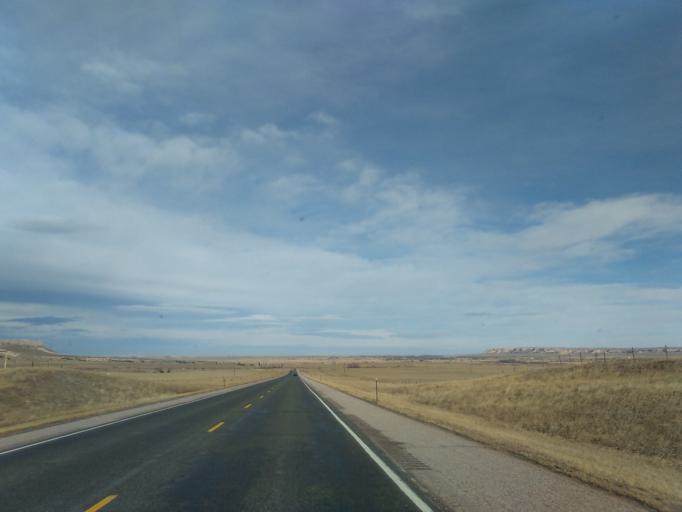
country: US
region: Wyoming
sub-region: Goshen County
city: Torrington
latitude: 41.6185
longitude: -104.2502
